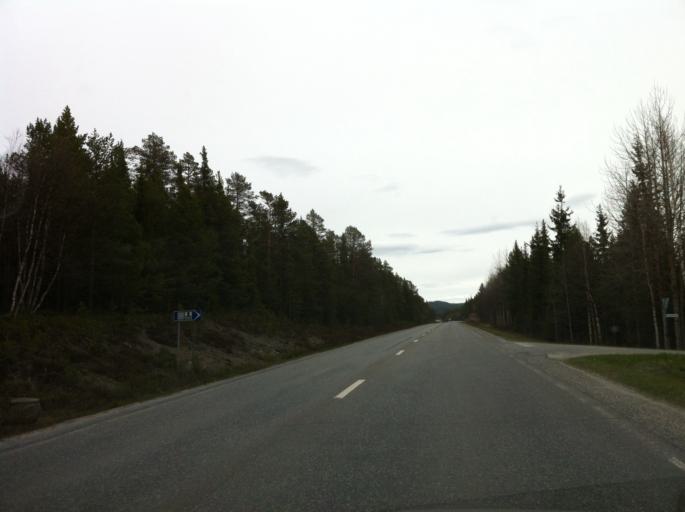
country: NO
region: Hedmark
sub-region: Engerdal
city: Engerdal
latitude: 62.5350
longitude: 12.5584
